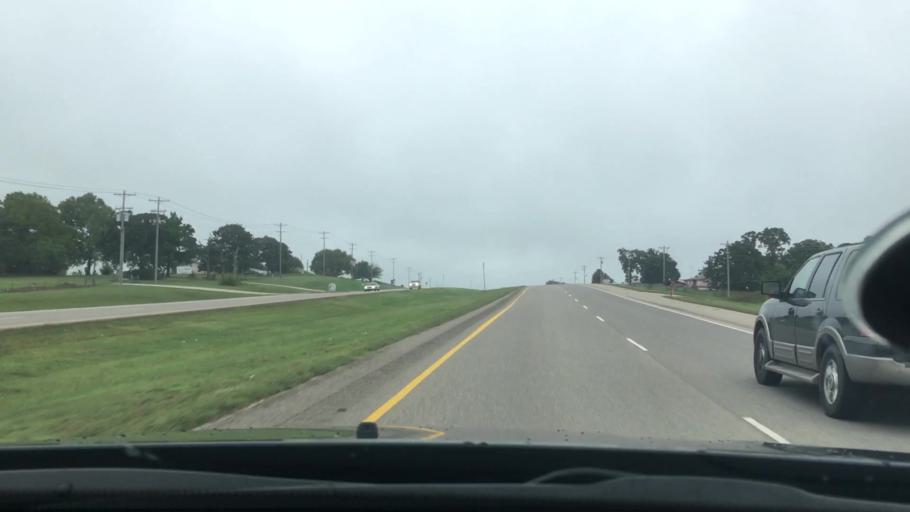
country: US
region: Oklahoma
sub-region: Seminole County
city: Seminole
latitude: 35.3126
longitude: -96.6714
